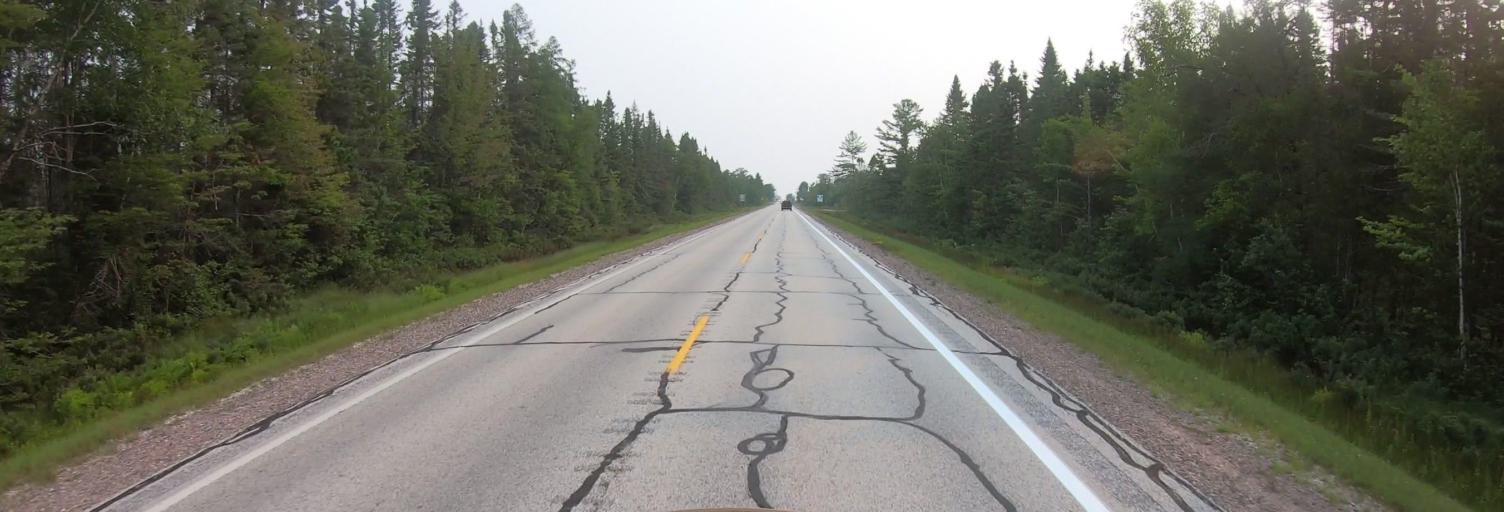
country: US
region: Michigan
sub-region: Luce County
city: Newberry
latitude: 46.5514
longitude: -85.0369
